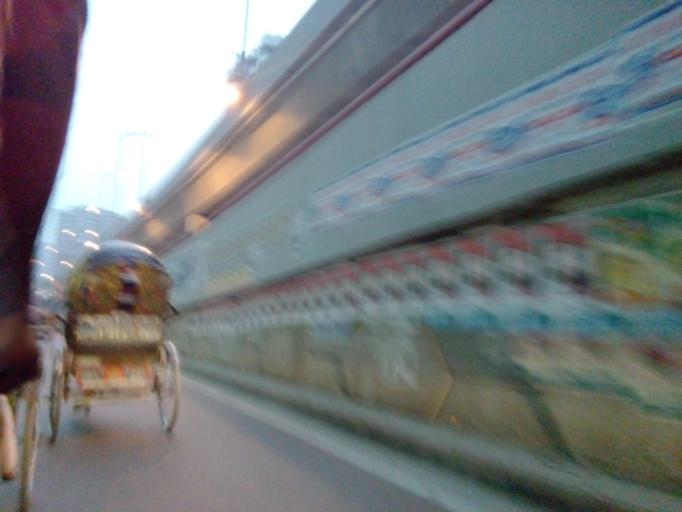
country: BD
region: Dhaka
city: Paltan
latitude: 23.7425
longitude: 90.4129
